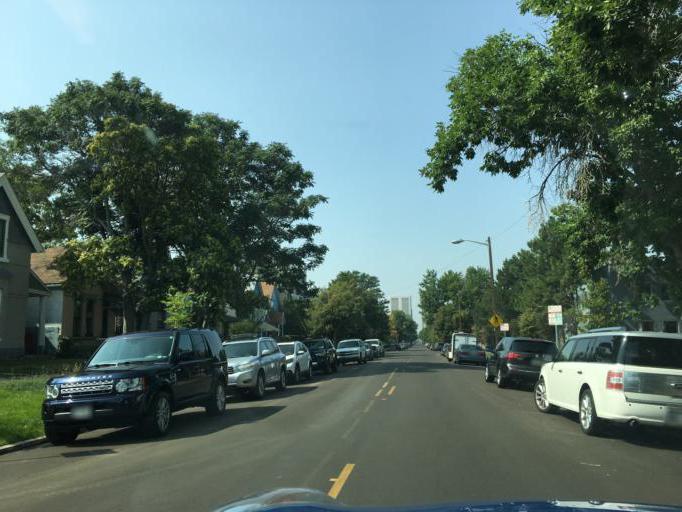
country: US
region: Colorado
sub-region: Denver County
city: Denver
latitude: 39.7616
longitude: -104.9779
